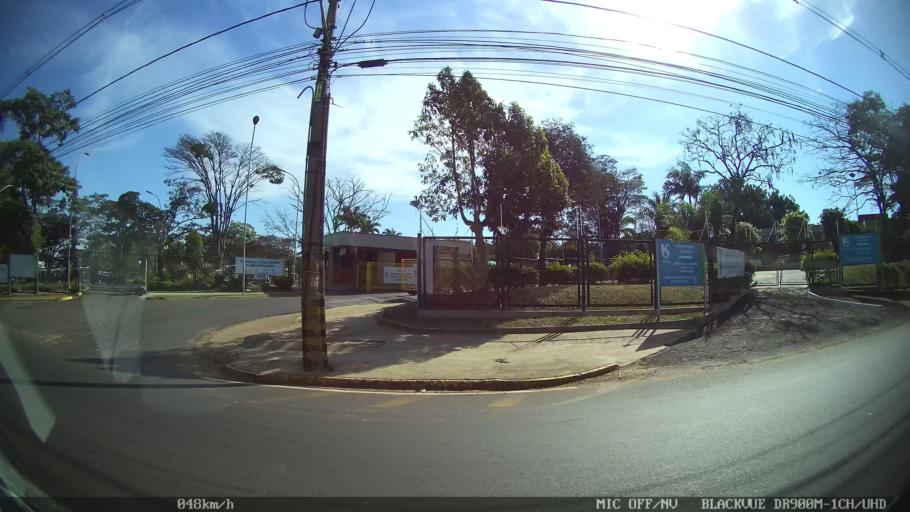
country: BR
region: Sao Paulo
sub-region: Franca
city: Franca
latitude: -20.5083
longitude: -47.4002
